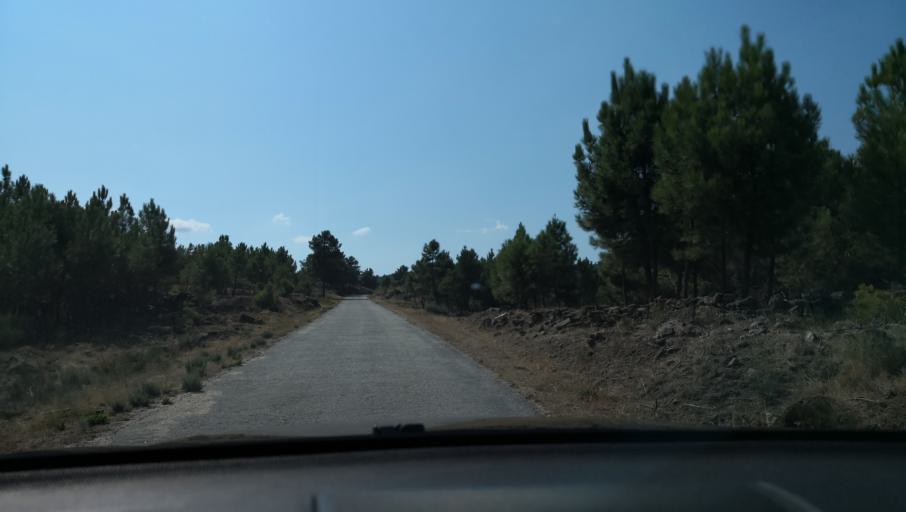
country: PT
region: Vila Real
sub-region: Sabrosa
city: Sabrosa
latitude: 41.3058
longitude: -7.5863
